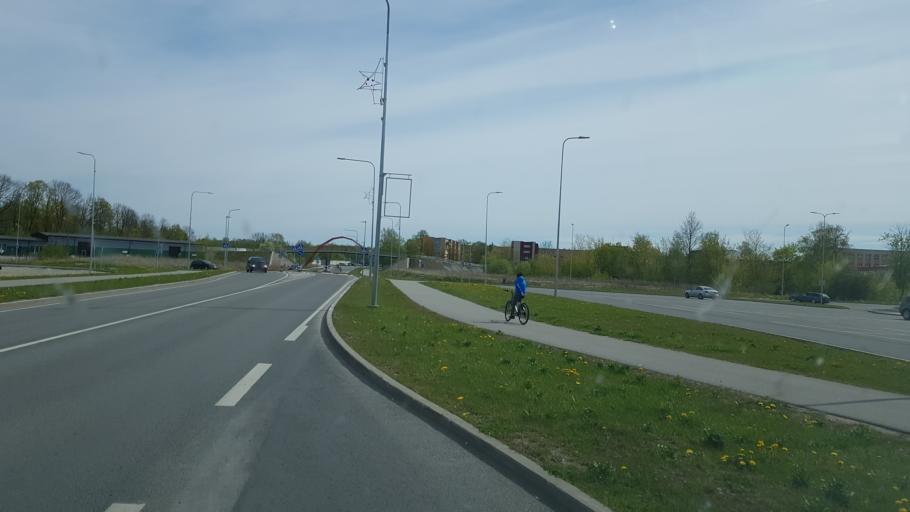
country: EE
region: Ida-Virumaa
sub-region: Johvi vald
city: Johvi
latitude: 59.3521
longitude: 27.4185
